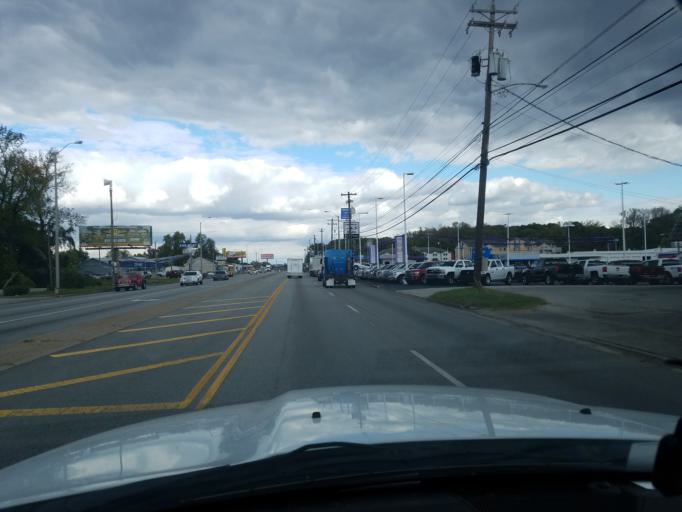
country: US
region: Kentucky
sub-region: Henderson County
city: Henderson
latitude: 37.8754
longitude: -87.5677
